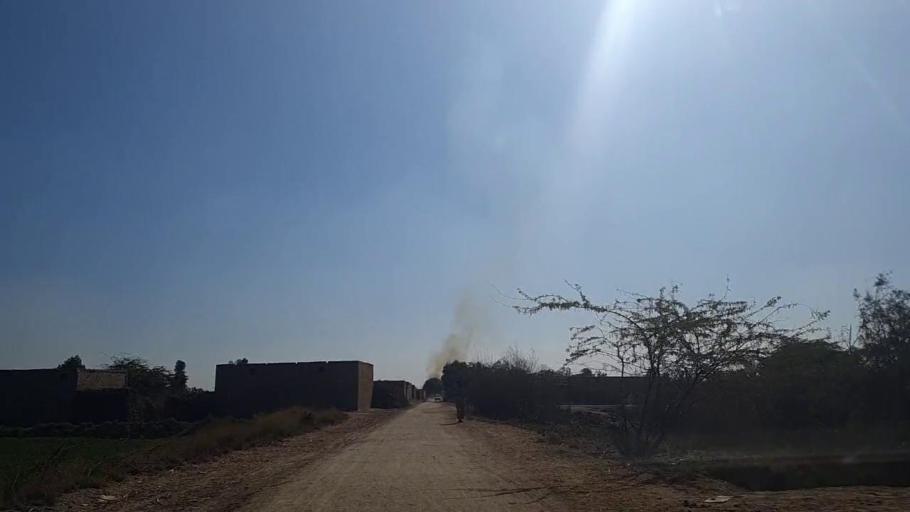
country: PK
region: Sindh
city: Sakrand
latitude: 26.2533
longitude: 68.1925
